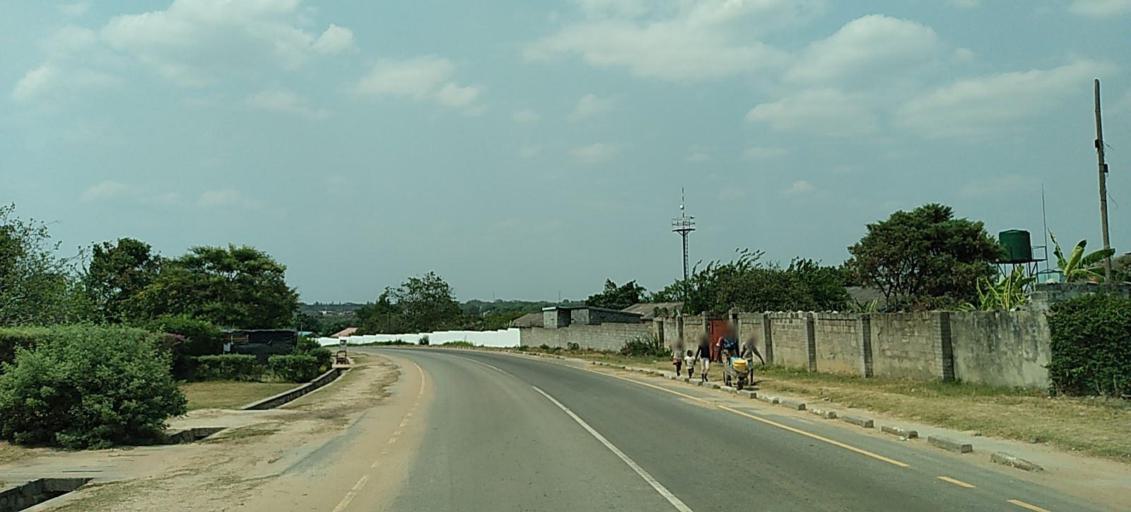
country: ZM
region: Copperbelt
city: Chambishi
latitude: -12.6344
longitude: 28.0580
